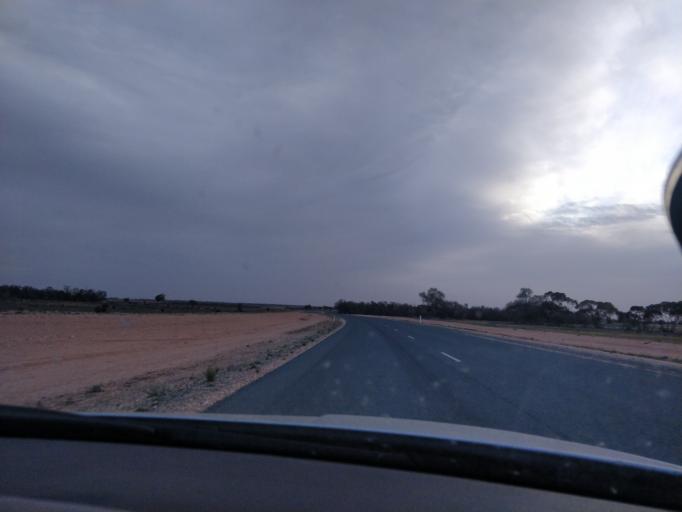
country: AU
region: New South Wales
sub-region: Wentworth
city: Gol Gol
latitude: -34.0360
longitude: 142.3575
